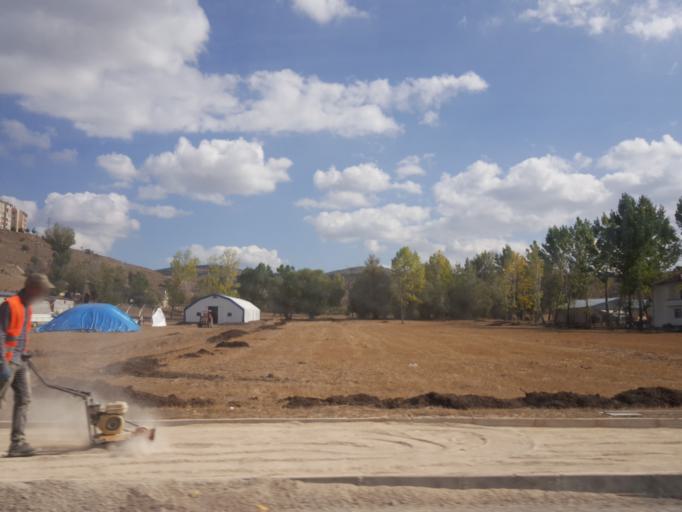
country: TR
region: Tokat
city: Artova
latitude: 40.1157
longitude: 36.3104
